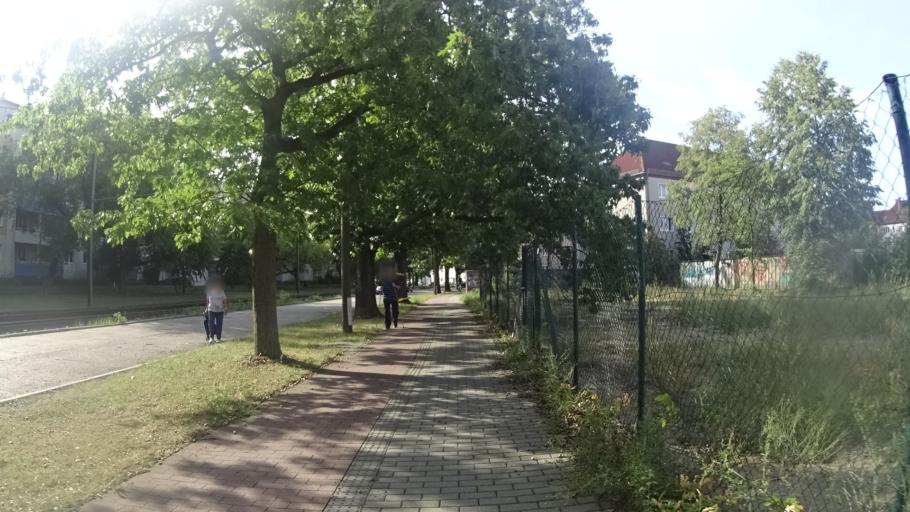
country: DE
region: Brandenburg
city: Brandenburg an der Havel
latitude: 52.4172
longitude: 12.5364
